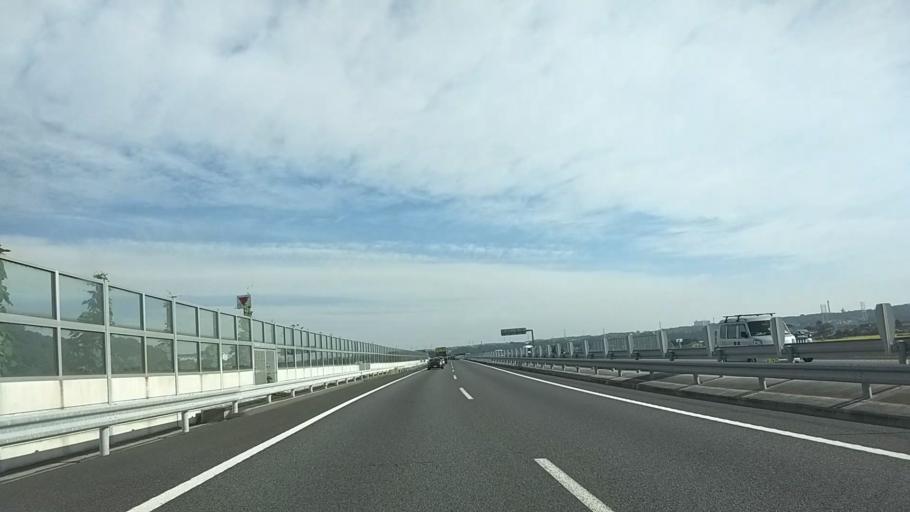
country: JP
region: Kanagawa
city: Zama
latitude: 35.5018
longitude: 139.3657
